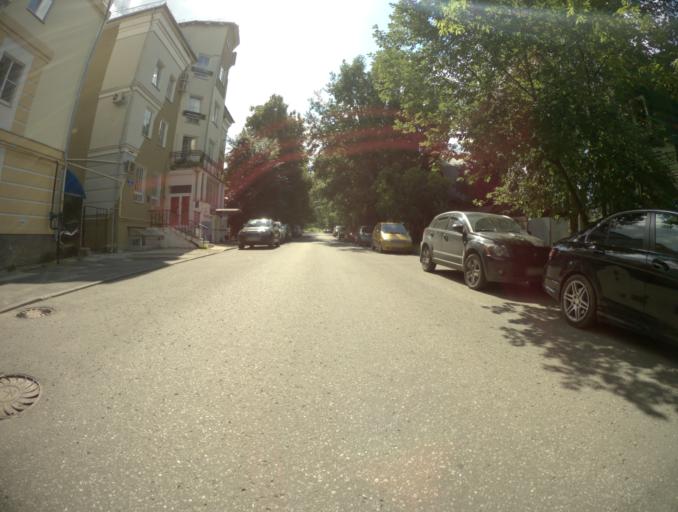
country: RU
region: Vladimir
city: Vladimir
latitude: 56.1330
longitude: 40.4086
